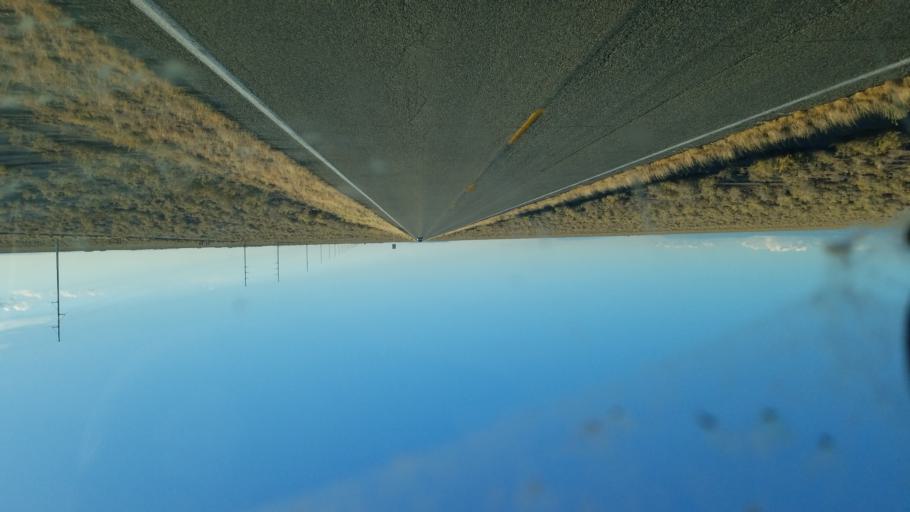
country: US
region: Colorado
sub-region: Saguache County
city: Center
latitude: 37.8474
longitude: -105.8916
